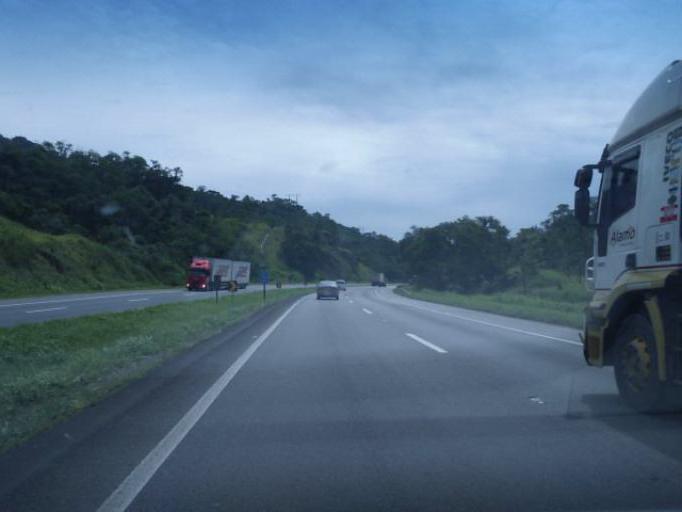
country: BR
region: Sao Paulo
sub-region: Miracatu
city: Miracatu
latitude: -24.3059
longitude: -47.4922
